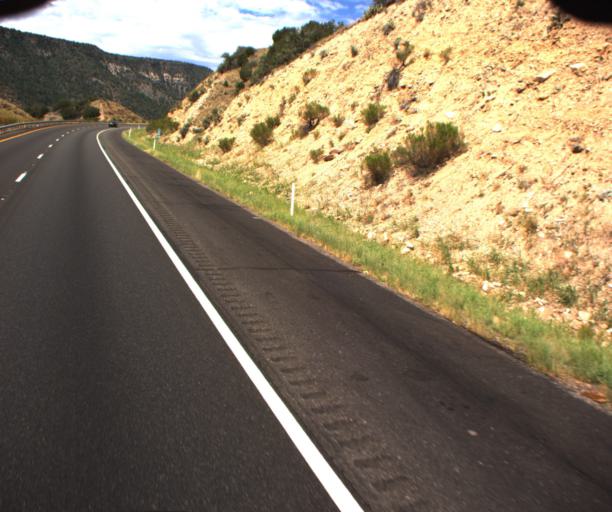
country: US
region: Arizona
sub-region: Yavapai County
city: Camp Verde
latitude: 34.5403
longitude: -111.9108
